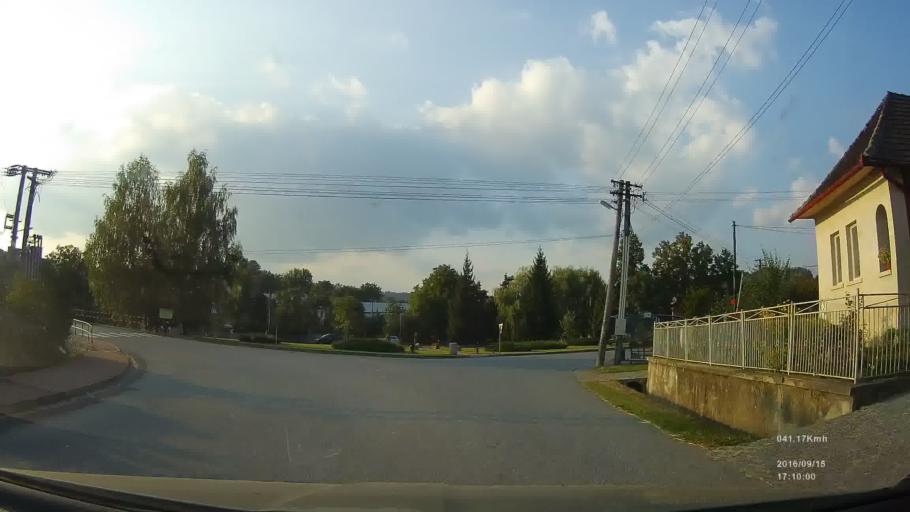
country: SK
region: Presovsky
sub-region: Okres Presov
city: Presov
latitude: 48.9178
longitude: 21.1188
